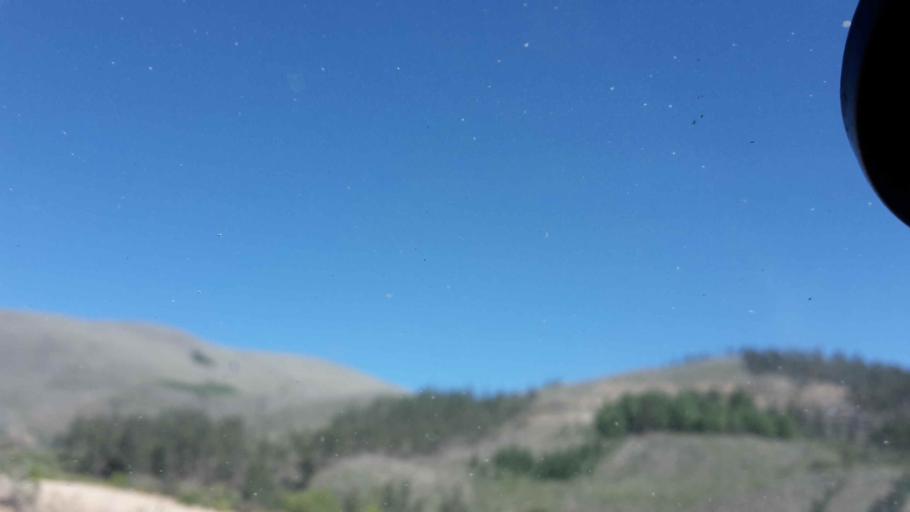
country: BO
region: Cochabamba
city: Arani
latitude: -17.6604
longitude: -65.7375
